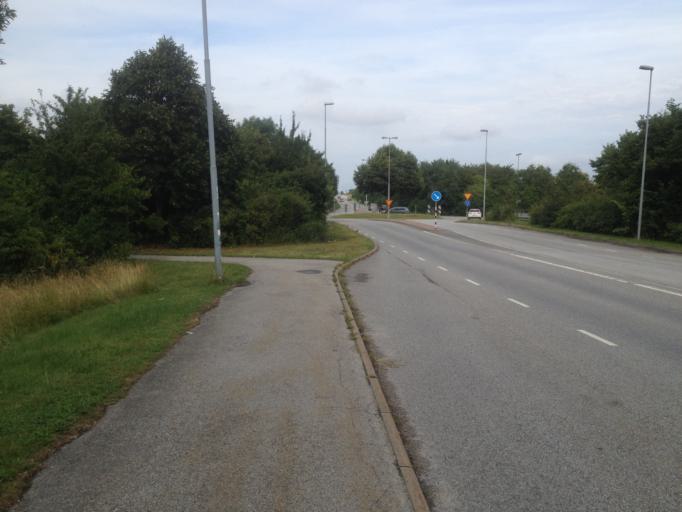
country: SE
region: Skane
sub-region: Lunds Kommun
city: Lund
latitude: 55.7038
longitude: 13.2427
